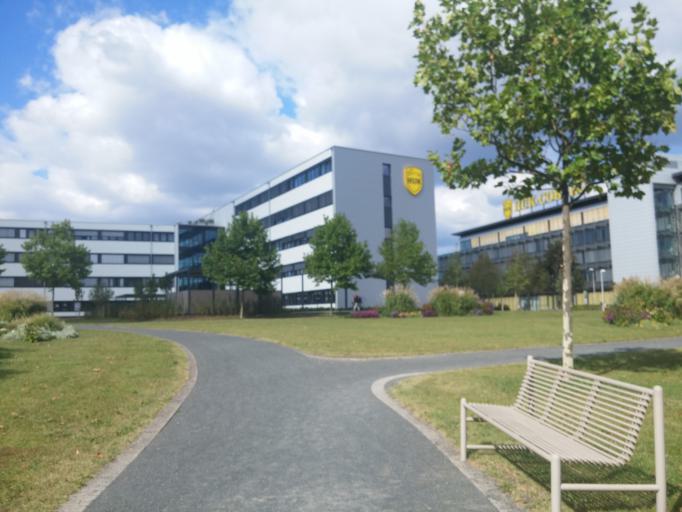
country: DE
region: Bavaria
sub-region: Upper Franconia
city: Coburg
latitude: 50.2817
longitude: 10.9736
